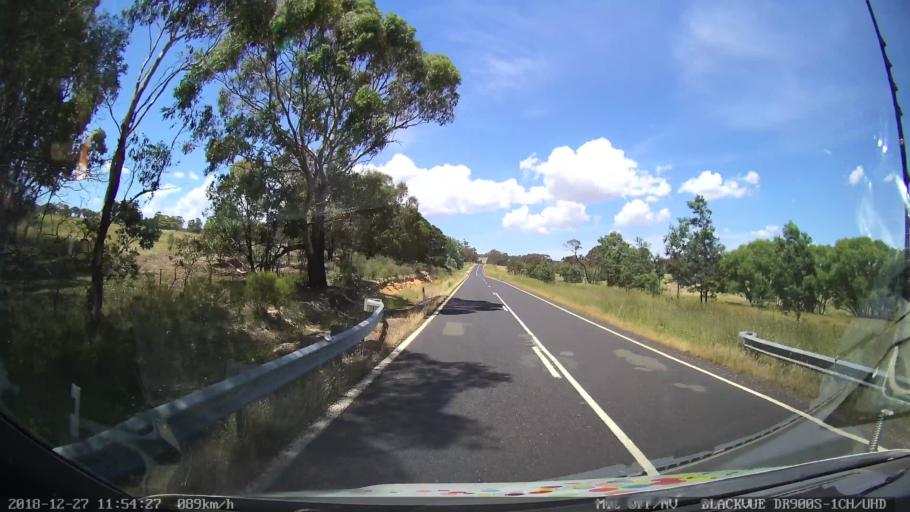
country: AU
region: New South Wales
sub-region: Blayney
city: Blayney
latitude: -33.6751
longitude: 149.4023
